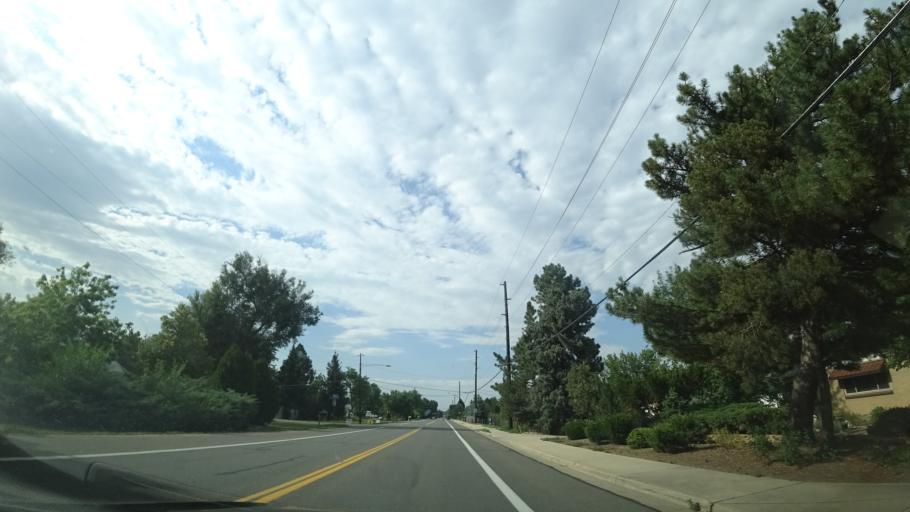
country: US
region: Colorado
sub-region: Jefferson County
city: Lakewood
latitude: 39.7150
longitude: -105.1002
